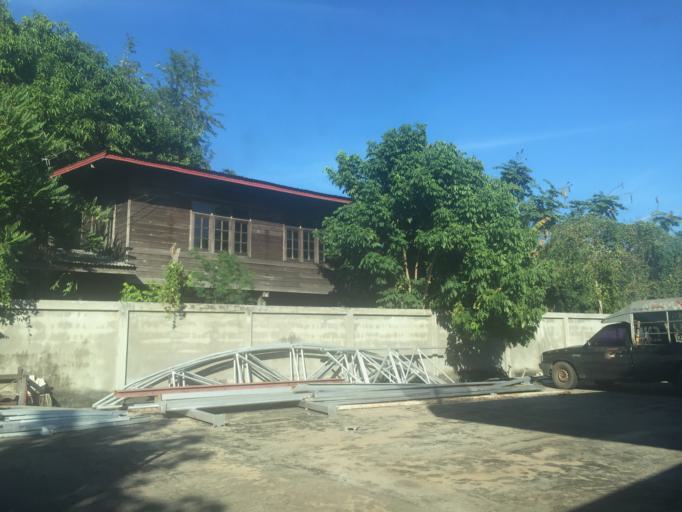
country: TH
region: Changwat Udon Thani
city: Si That
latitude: 16.9766
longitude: 103.1973
